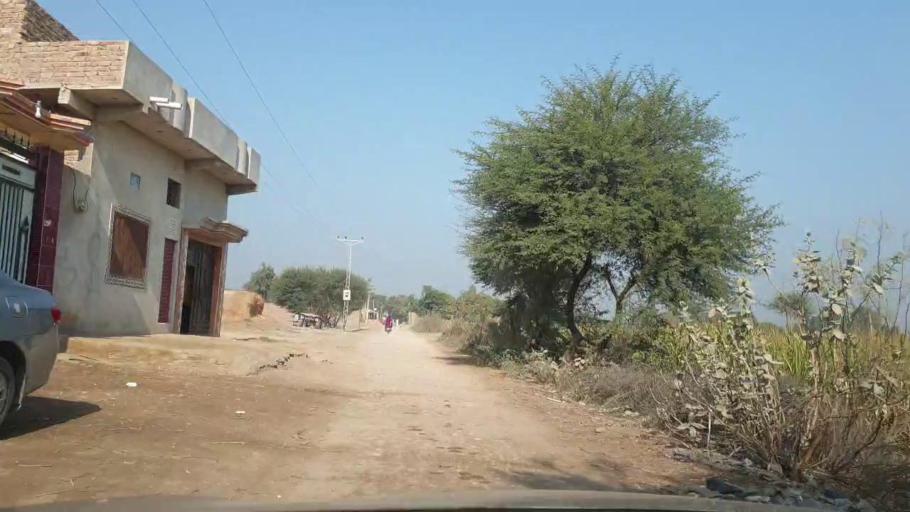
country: PK
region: Sindh
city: Tando Allahyar
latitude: 25.5010
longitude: 68.7534
